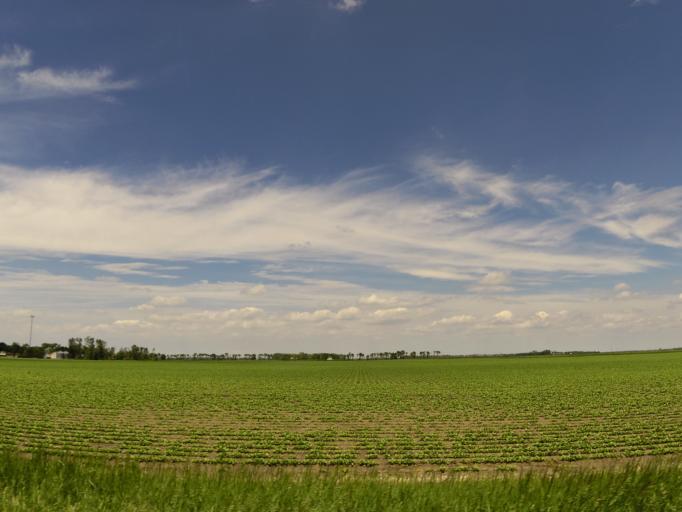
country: US
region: North Dakota
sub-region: Walsh County
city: Grafton
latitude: 48.2954
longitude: -97.2134
